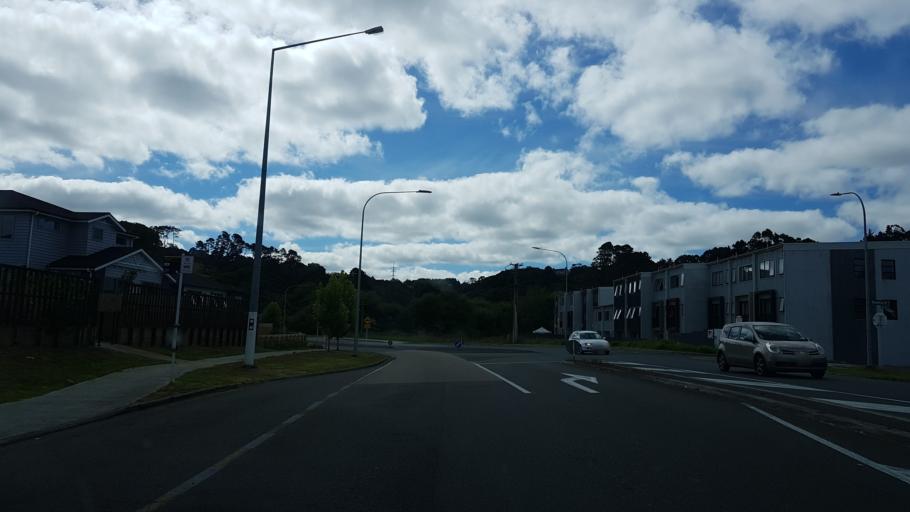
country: NZ
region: Auckland
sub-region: Auckland
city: Rothesay Bay
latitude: -36.7222
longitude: 174.6913
